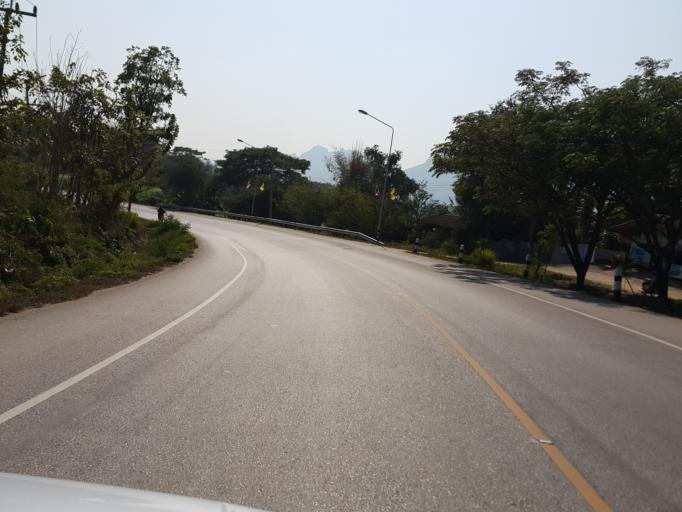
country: TH
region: Lampang
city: Chae Hom
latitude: 18.7720
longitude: 99.5732
